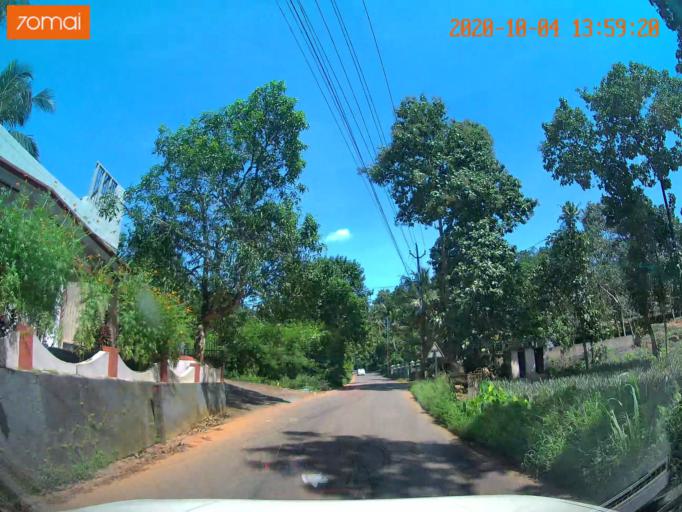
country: IN
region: Kerala
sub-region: Kottayam
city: Lalam
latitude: 9.7173
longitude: 76.6618
